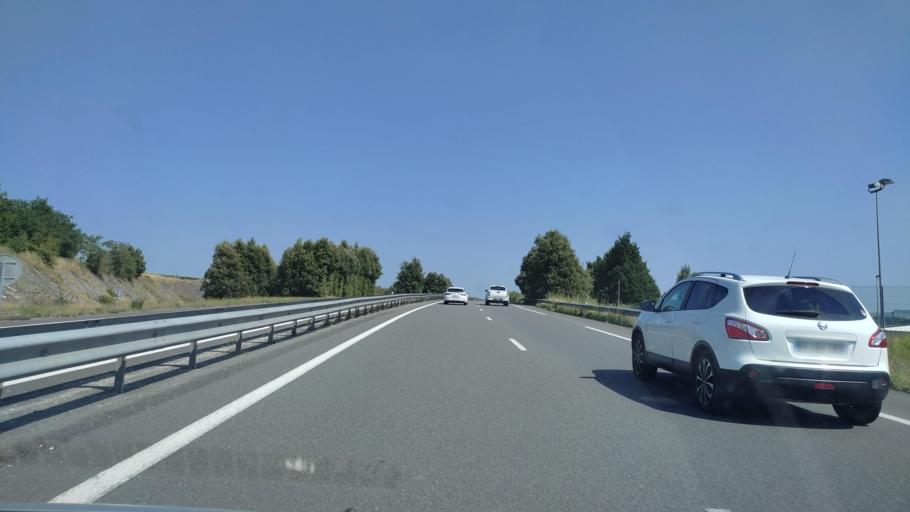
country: FR
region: Poitou-Charentes
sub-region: Departement de la Charente
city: Gensac-la-Pallue
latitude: 45.6649
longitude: -0.2341
